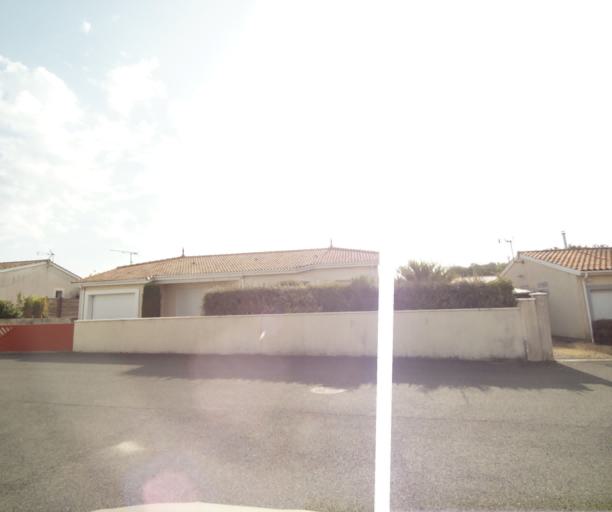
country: FR
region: Aquitaine
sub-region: Departement de la Gironde
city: Creon
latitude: 44.7690
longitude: -0.3497
